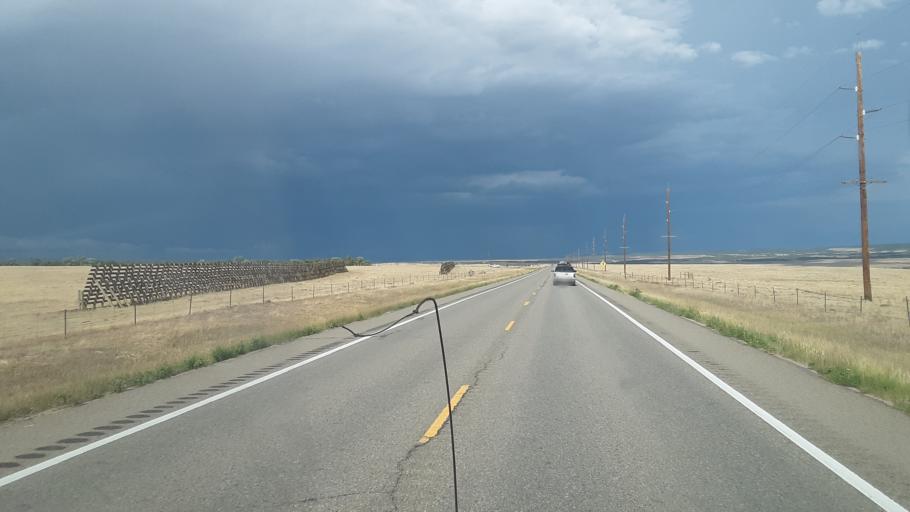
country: US
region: Colorado
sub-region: Huerfano County
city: Walsenburg
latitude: 37.5434
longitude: -105.0244
